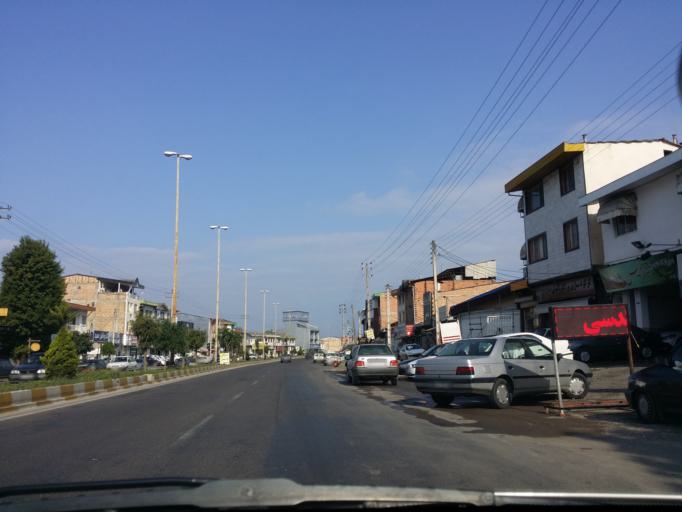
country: IR
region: Mazandaran
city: Chalus
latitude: 36.6776
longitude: 51.4037
